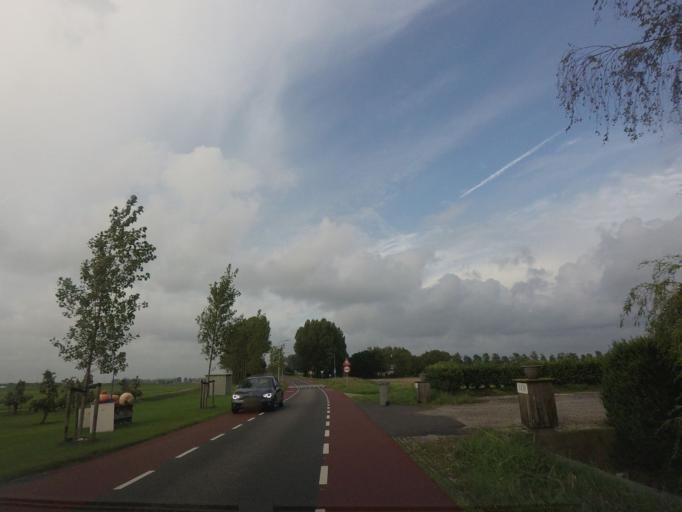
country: NL
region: South Holland
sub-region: Gemeente Kaag en Braassem
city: Oude Wetering
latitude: 52.2423
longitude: 4.6421
